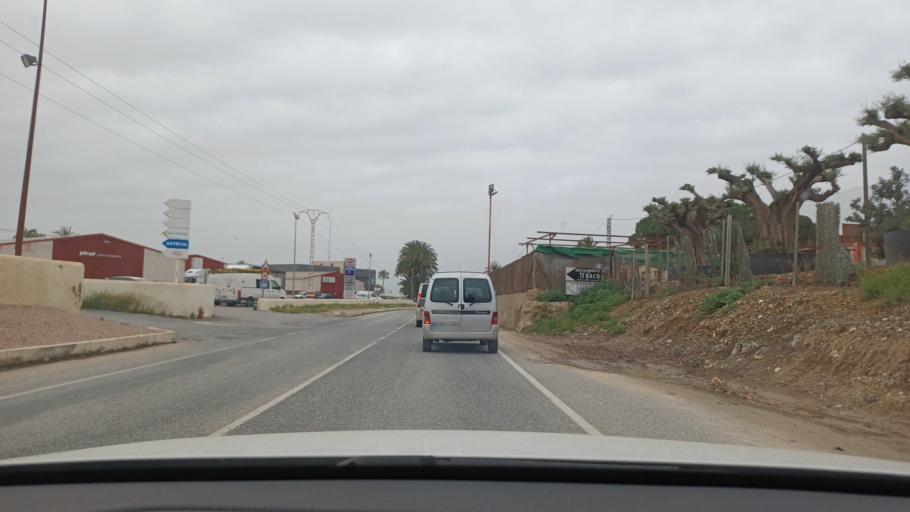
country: ES
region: Valencia
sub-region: Provincia de Alicante
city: Elche
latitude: 38.2422
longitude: -0.7087
